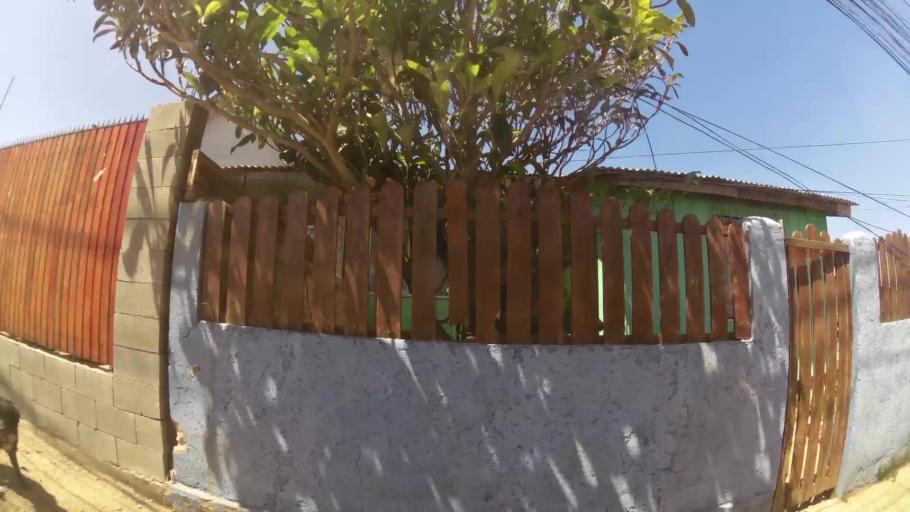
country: CL
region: Valparaiso
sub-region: Provincia de Valparaiso
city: Valparaiso
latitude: -33.0314
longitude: -71.6534
